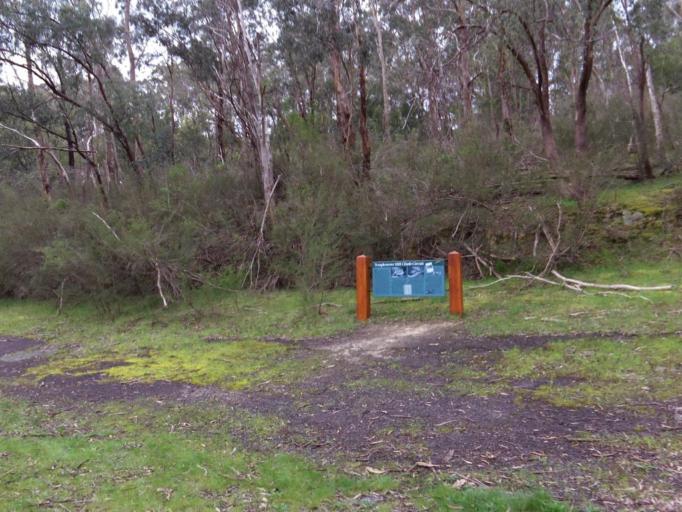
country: AU
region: Victoria
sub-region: Nillumbik
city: Eltham
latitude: -37.7439
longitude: 145.1716
